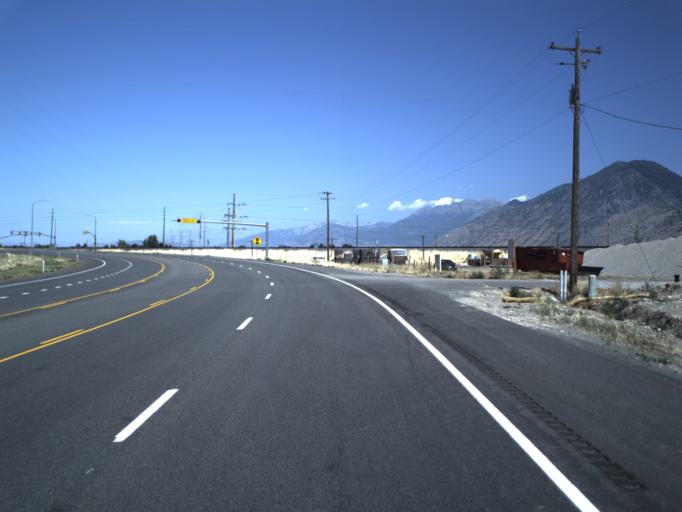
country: US
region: Utah
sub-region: Utah County
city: Mapleton
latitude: 40.0877
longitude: -111.5933
